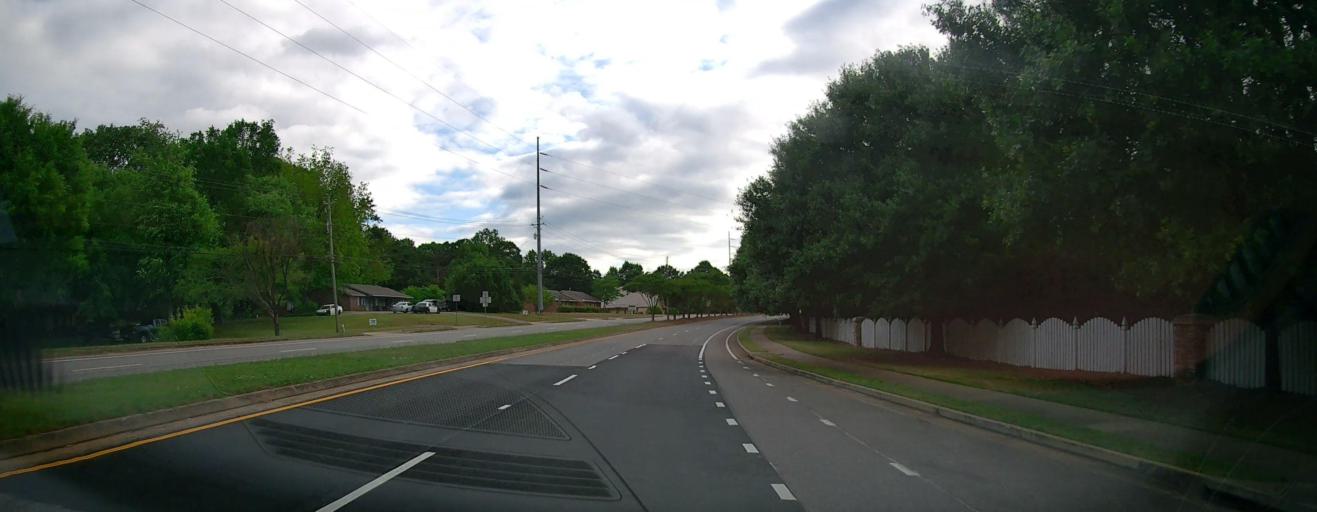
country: US
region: Georgia
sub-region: Clarke County
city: Country Club Estates
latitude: 33.9383
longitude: -83.4331
